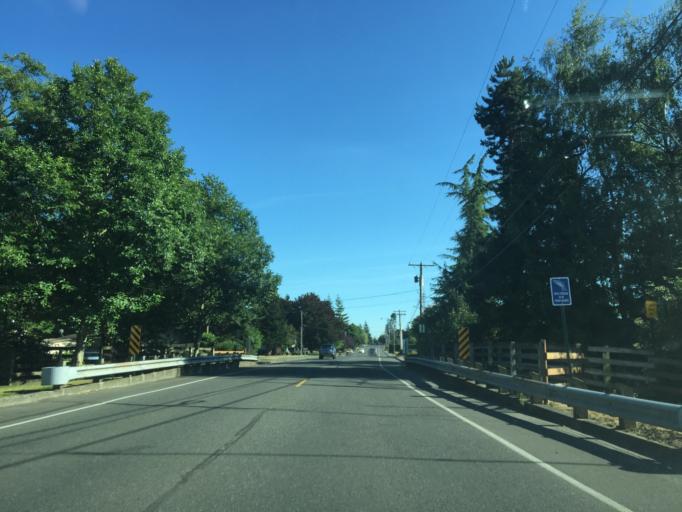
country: US
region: Washington
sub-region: Whatcom County
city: Lynden
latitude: 48.9559
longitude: -122.4413
